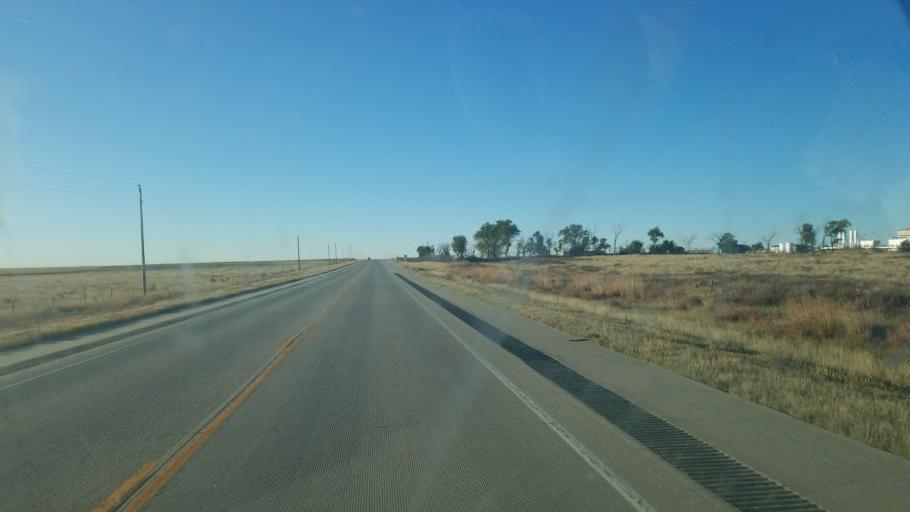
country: US
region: Colorado
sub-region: Kiowa County
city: Eads
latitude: 38.6629
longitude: -102.7860
